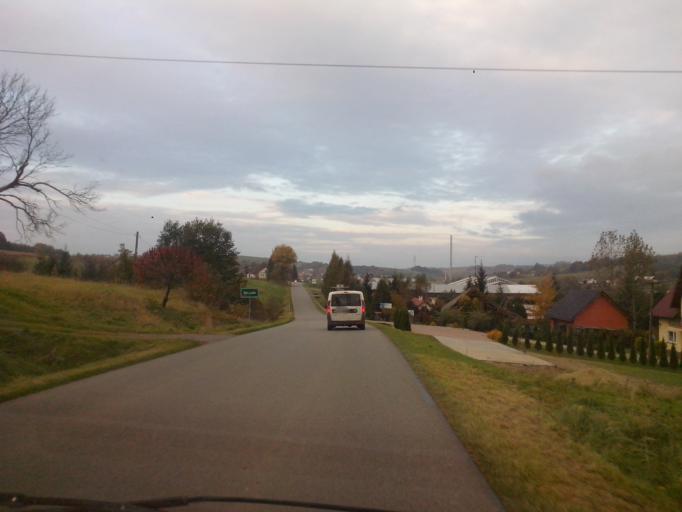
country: PL
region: Subcarpathian Voivodeship
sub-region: Powiat ropczycko-sedziszowski
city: Wielopole Skrzynskie
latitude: 49.9477
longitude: 21.6275
